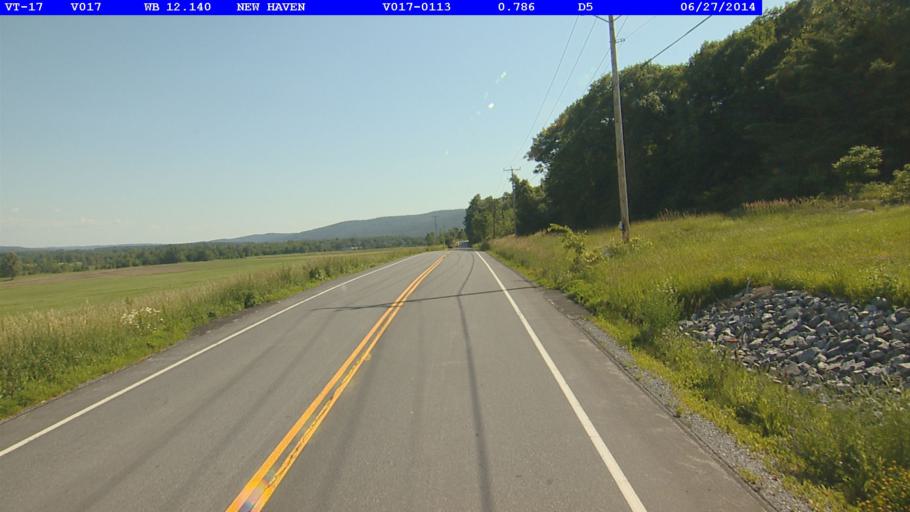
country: US
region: Vermont
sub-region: Addison County
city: Vergennes
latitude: 44.0913
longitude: -73.2338
